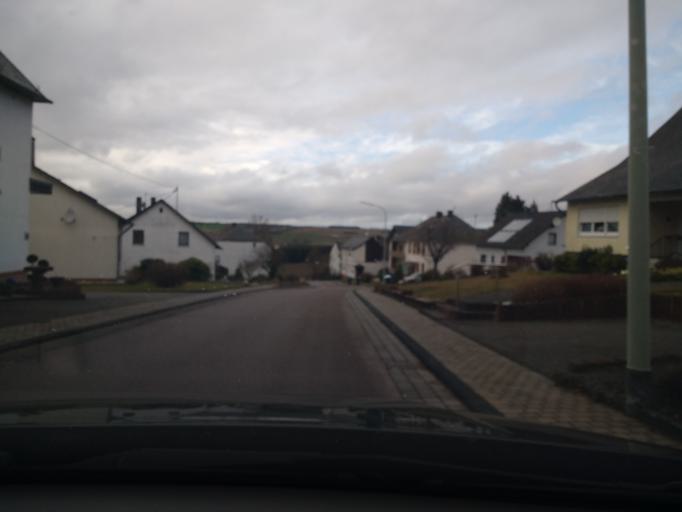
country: DE
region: Rheinland-Pfalz
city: Waldweiler
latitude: 49.6145
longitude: 6.7963
